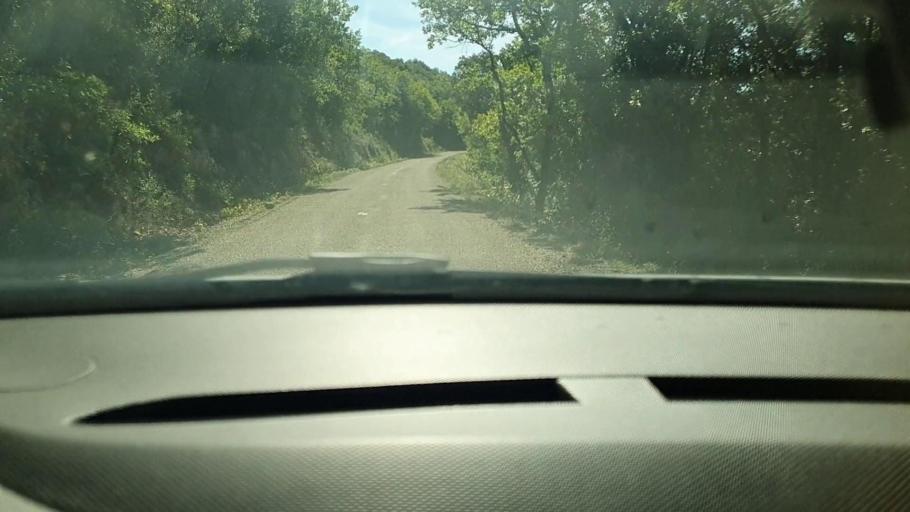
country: FR
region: Languedoc-Roussillon
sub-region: Departement du Gard
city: Barjac
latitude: 44.2029
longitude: 4.3134
